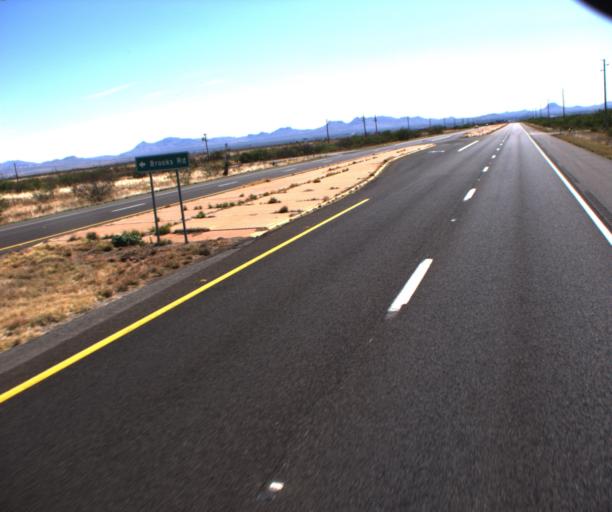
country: US
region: Arizona
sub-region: Cochise County
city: Pirtleville
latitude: 31.3608
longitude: -109.6658
